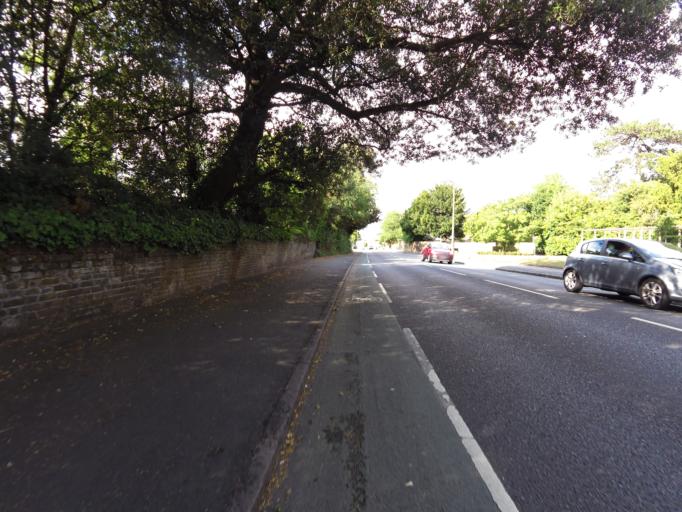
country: GB
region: England
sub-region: Hertfordshire
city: Hoddesdon
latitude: 51.7540
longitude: -0.0141
